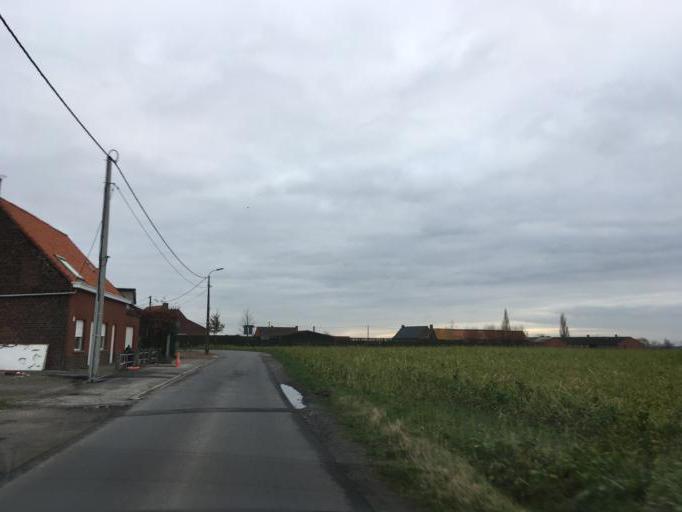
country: BE
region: Flanders
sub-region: Provincie West-Vlaanderen
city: Ledegem
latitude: 50.8909
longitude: 3.1364
